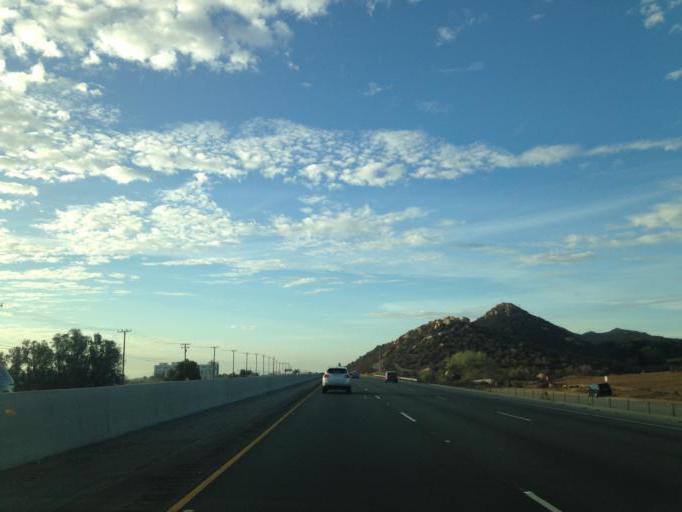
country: US
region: California
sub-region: Riverside County
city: Murrieta Hot Springs
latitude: 33.6233
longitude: -117.1712
